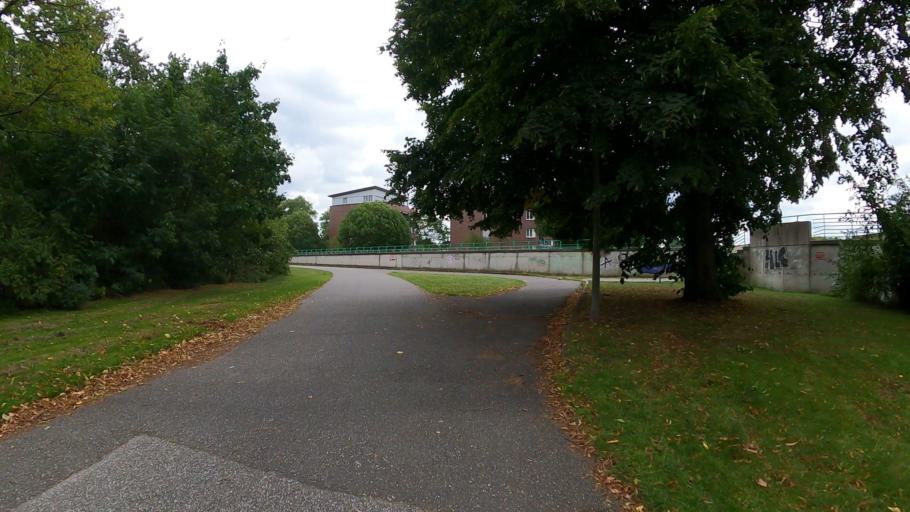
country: DE
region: Hamburg
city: Altona
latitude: 53.5385
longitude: 9.8698
